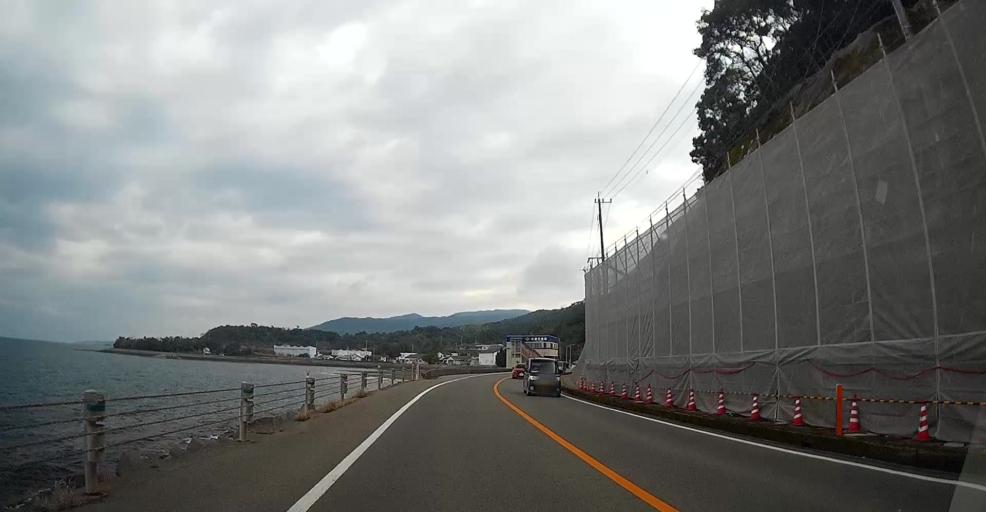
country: JP
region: Kumamoto
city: Hondo
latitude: 32.4572
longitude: 130.2194
